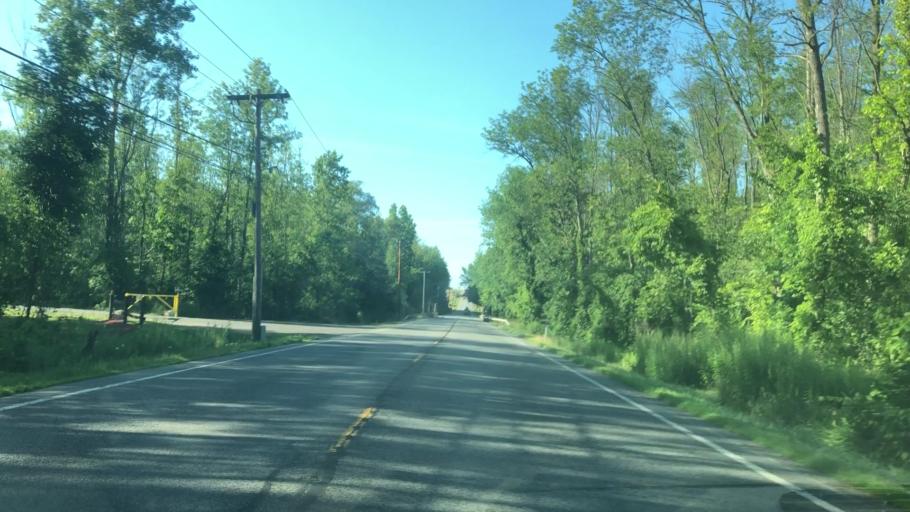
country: US
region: New York
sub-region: Wayne County
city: Macedon
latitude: 43.1285
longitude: -77.2926
